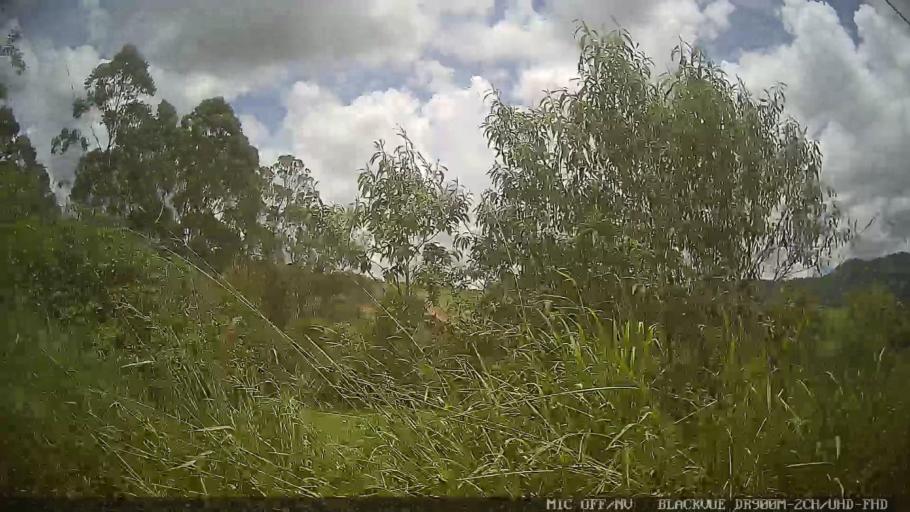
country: BR
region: Sao Paulo
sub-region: Atibaia
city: Atibaia
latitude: -23.0361
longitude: -46.5413
